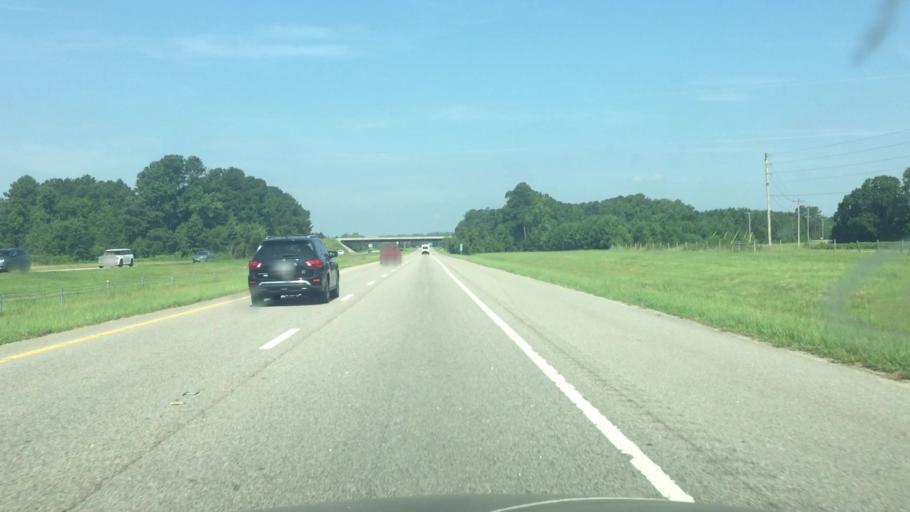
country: US
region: North Carolina
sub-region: Robeson County
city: Lumberton
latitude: 34.5879
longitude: -79.0635
